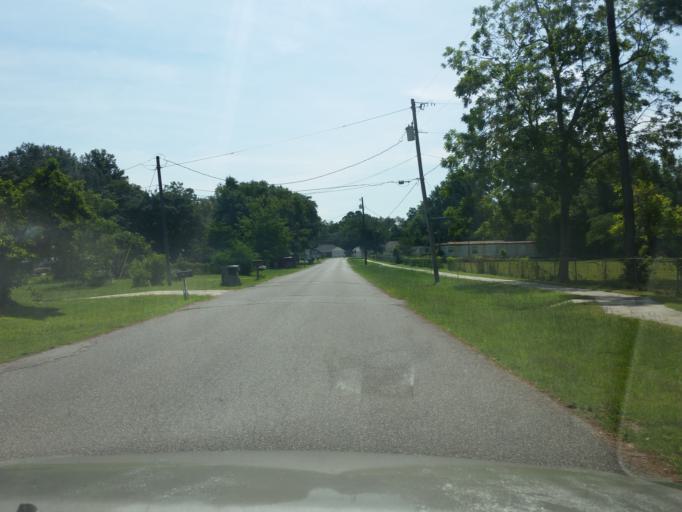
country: US
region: Florida
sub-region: Escambia County
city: Ferry Pass
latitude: 30.5144
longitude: -87.1965
